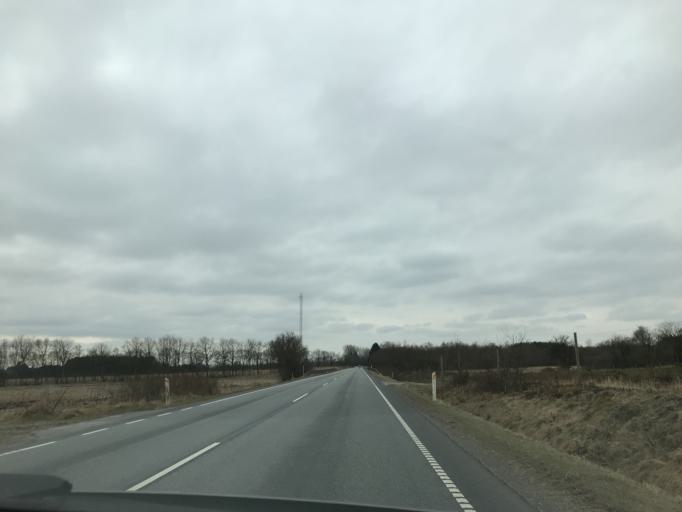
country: DK
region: South Denmark
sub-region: Varde Kommune
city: Olgod
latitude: 55.8151
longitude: 8.6688
